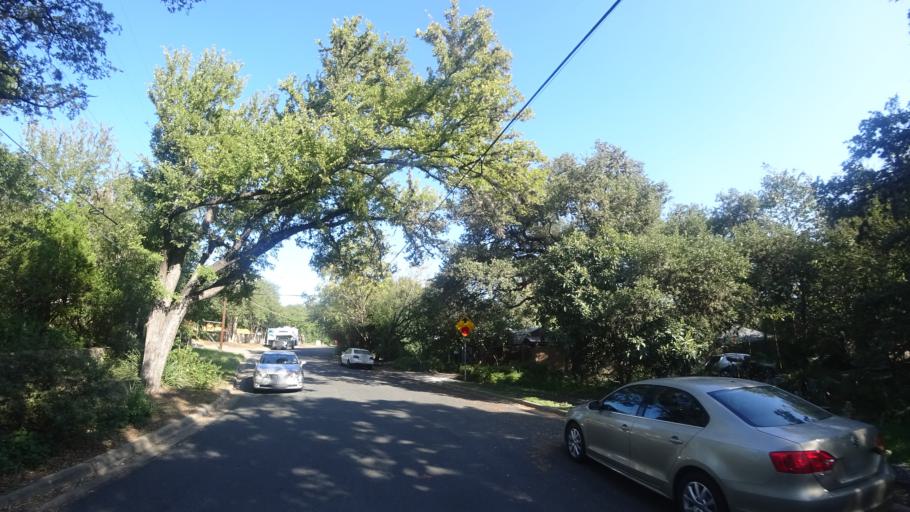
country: US
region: Texas
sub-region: Travis County
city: Austin
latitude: 30.2507
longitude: -97.7434
